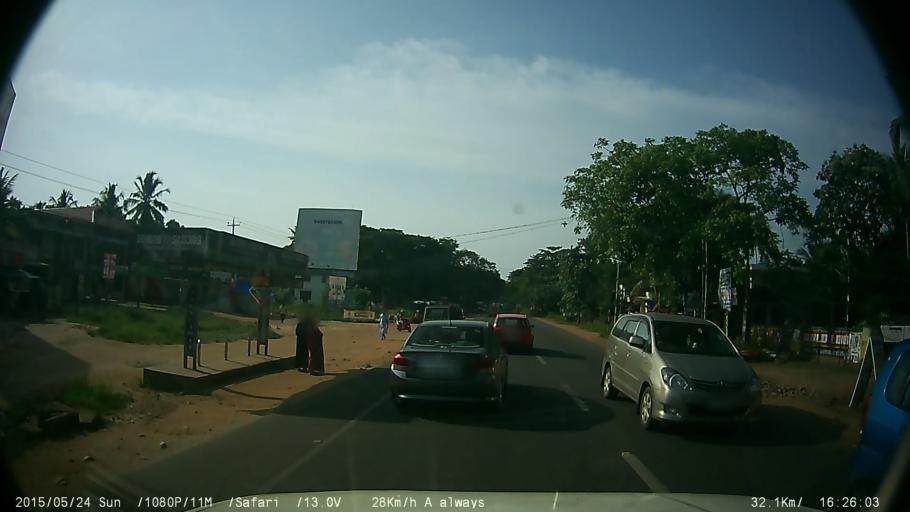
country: IN
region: Kerala
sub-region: Alappuzha
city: Alleppey
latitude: 9.5166
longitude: 76.3278
